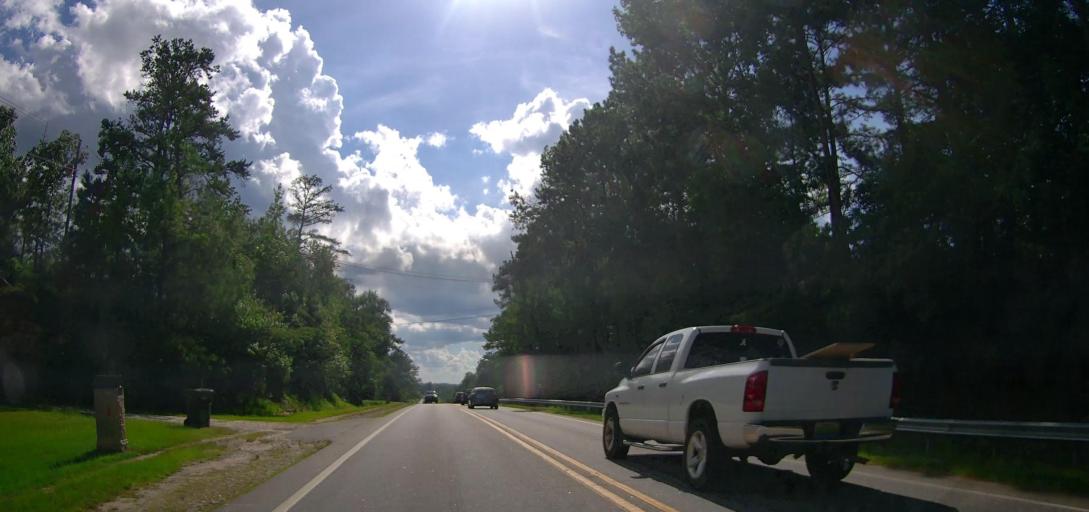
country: US
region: Alabama
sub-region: Russell County
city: Ladonia
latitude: 32.4627
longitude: -85.1261
